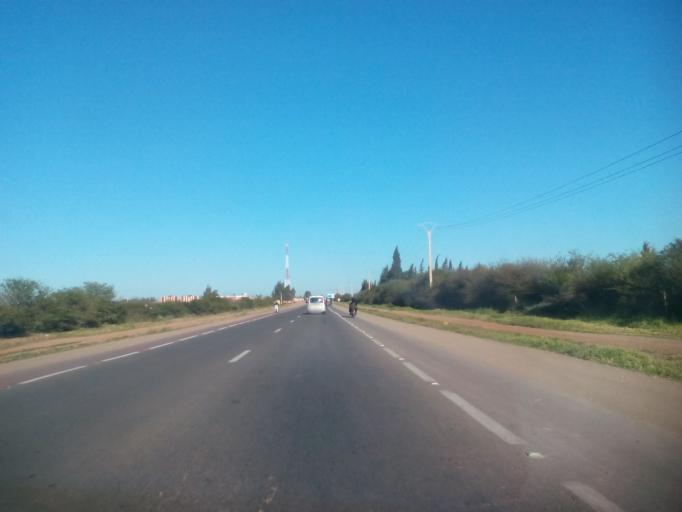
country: MA
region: Marrakech-Tensift-Al Haouz
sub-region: Marrakech
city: Marrakesh
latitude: 31.6309
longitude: -8.1720
